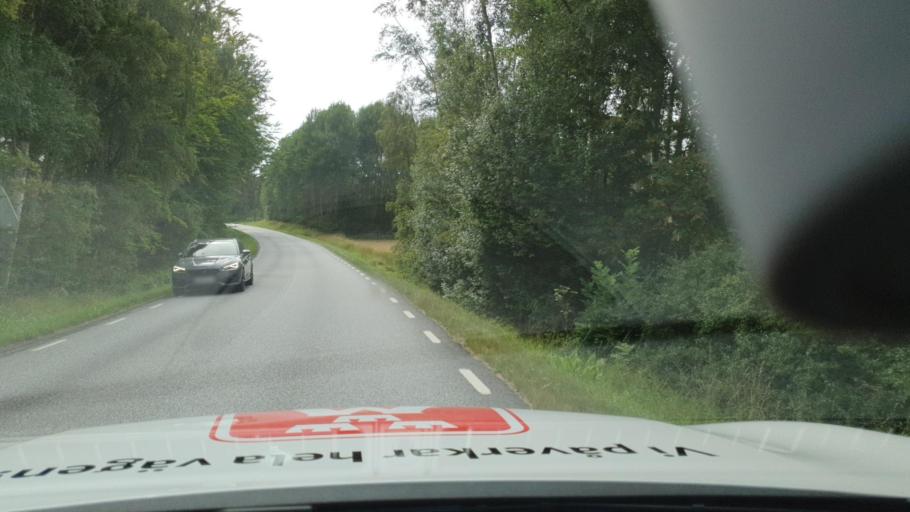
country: SE
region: Vaestra Goetaland
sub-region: Sotenas Kommun
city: Hunnebostrand
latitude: 58.5640
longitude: 11.2868
